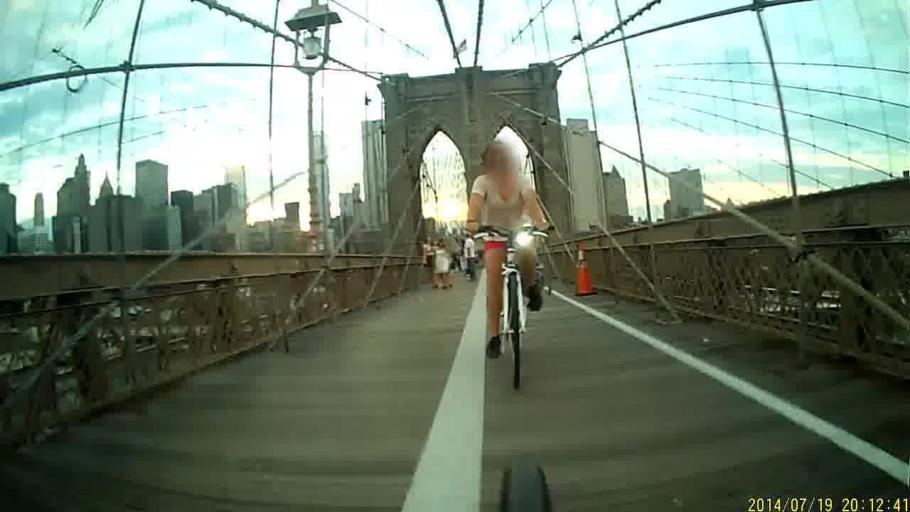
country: US
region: New York
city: New York City
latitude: 40.7064
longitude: -73.9970
